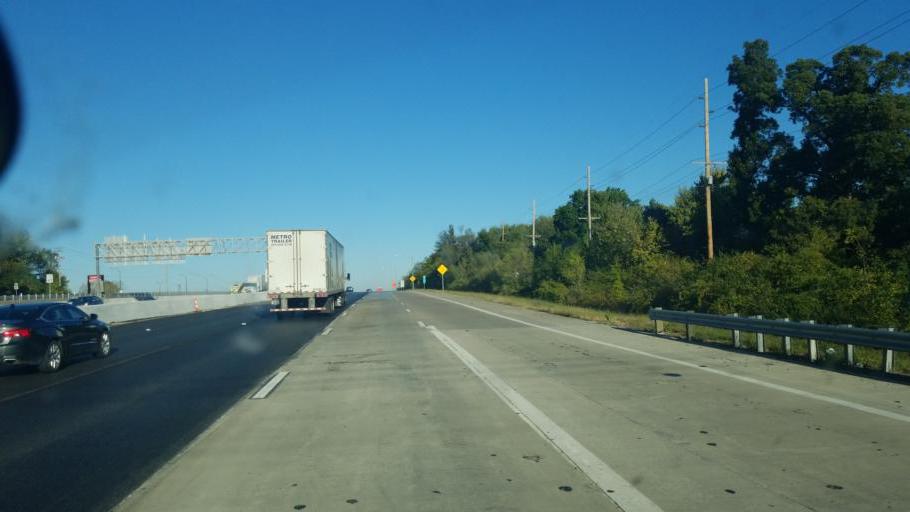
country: US
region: Missouri
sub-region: Saint Charles County
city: Saint Charles
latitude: 38.7783
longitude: -90.5138
